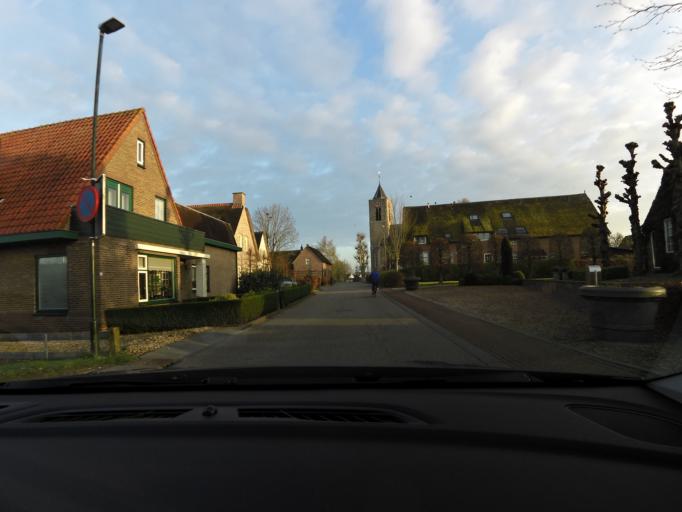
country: NL
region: South Holland
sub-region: Gemeente Gorinchem
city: Gorinchem
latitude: 51.8794
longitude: 4.9470
